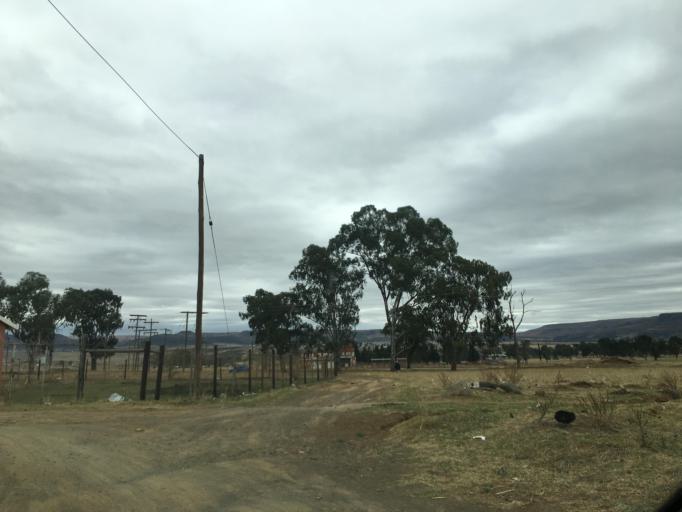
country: ZA
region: Eastern Cape
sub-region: Chris Hani District Municipality
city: Cala
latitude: -31.5338
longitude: 27.6904
